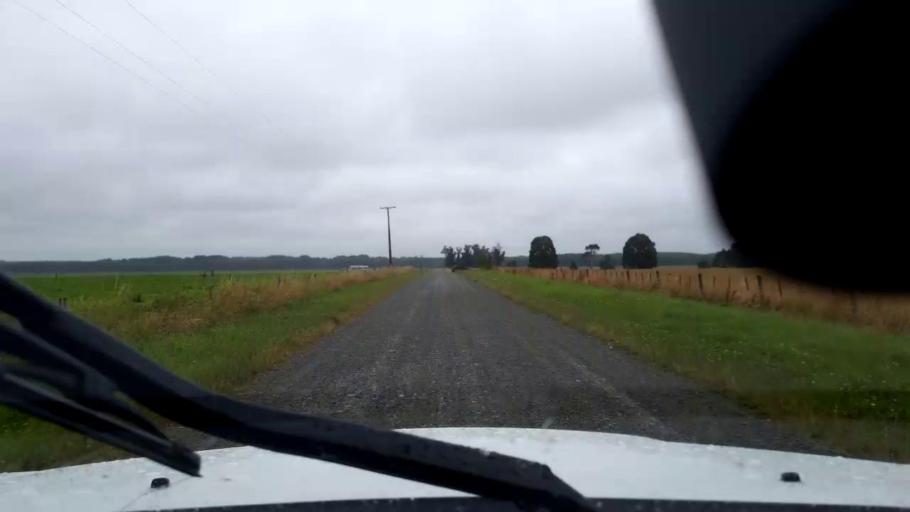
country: NZ
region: Canterbury
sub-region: Timaru District
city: Pleasant Point
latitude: -44.2449
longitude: 171.2011
